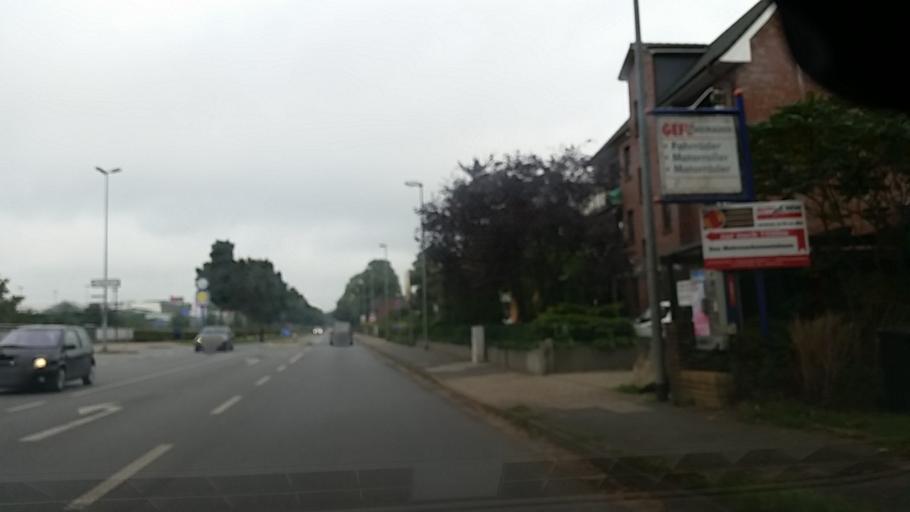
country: DE
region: Schleswig-Holstein
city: Henstedt-Ulzburg
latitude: 53.7985
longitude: 9.9834
